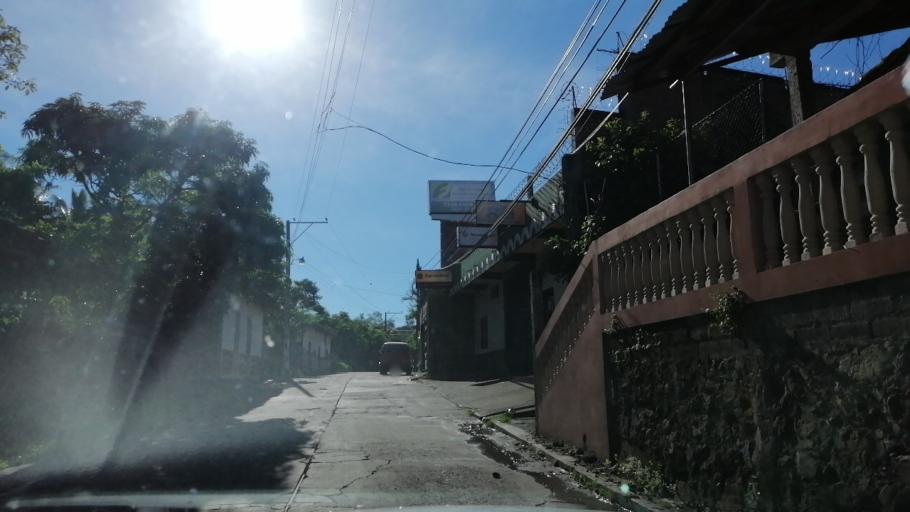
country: SV
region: Morazan
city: Cacaopera
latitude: 13.7725
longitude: -88.0792
